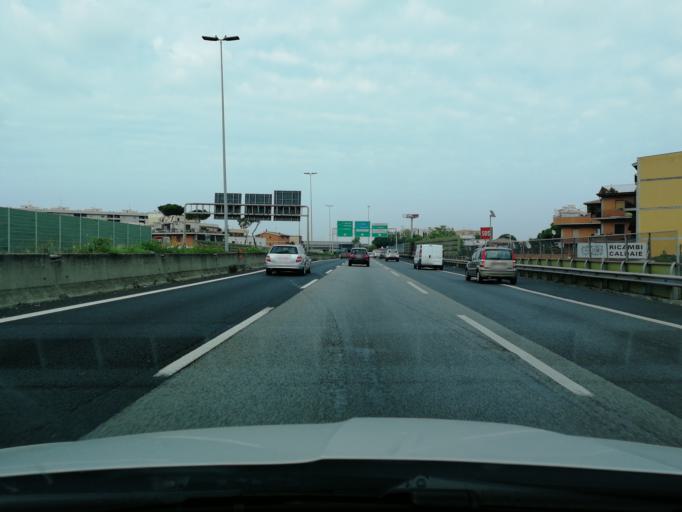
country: IT
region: Latium
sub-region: Citta metropolitana di Roma Capitale
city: Ciampino
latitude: 41.8450
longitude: 12.5944
